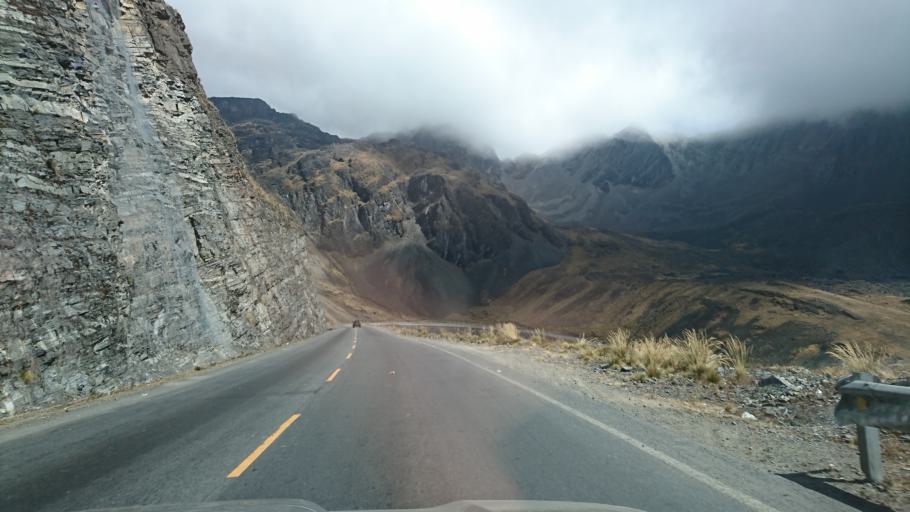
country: BO
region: La Paz
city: La Paz
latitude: -16.3206
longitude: -68.0323
